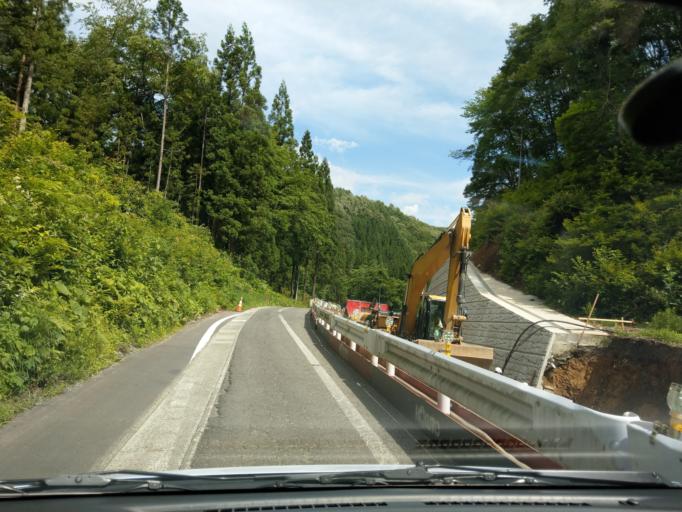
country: JP
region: Akita
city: Kakunodatemachi
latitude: 39.7220
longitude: 140.5830
